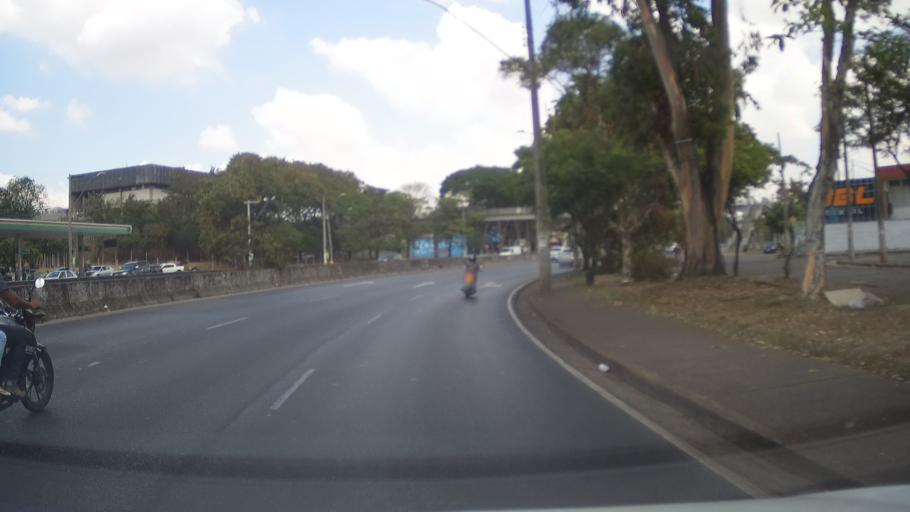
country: BR
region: Minas Gerais
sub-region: Belo Horizonte
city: Belo Horizonte
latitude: -19.9206
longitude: -43.9700
